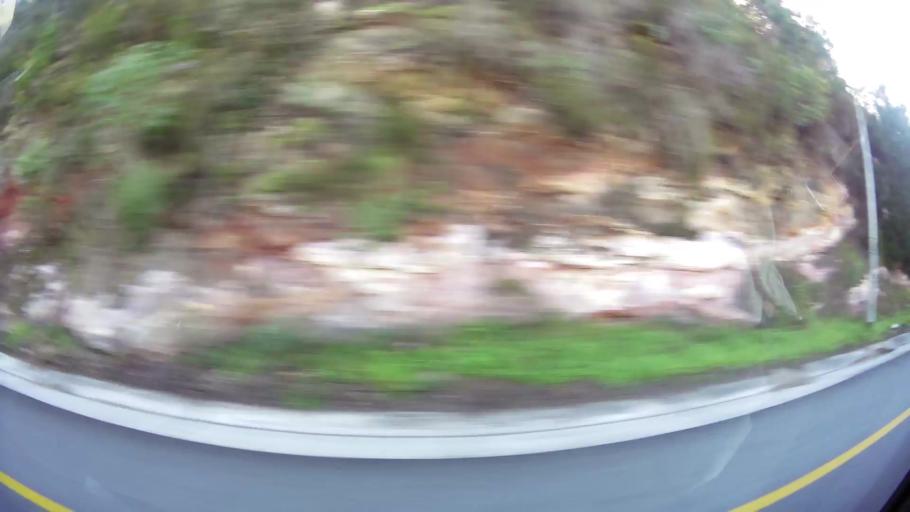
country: ZA
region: Western Cape
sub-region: Eden District Municipality
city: Knysna
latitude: -34.0371
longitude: 23.0242
